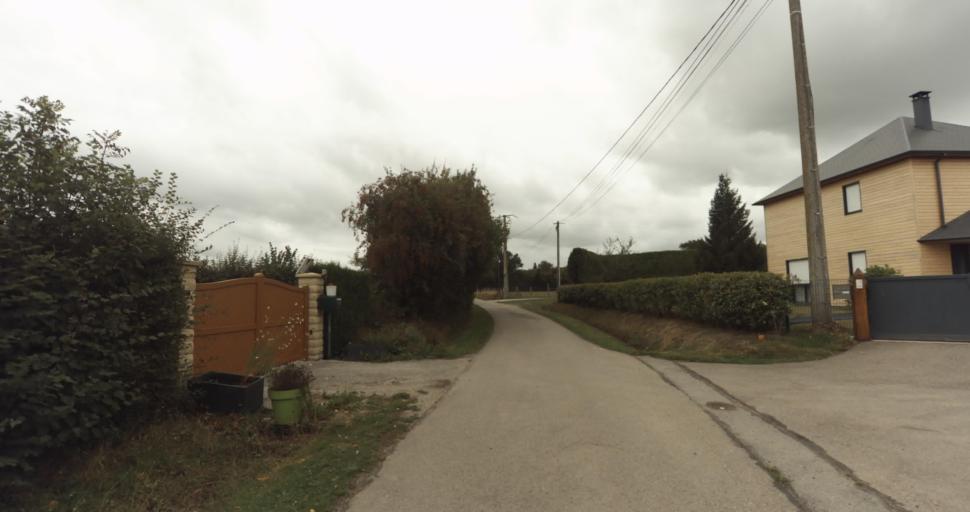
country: FR
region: Lower Normandy
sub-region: Departement de l'Orne
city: Gace
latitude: 48.8108
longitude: 0.3516
